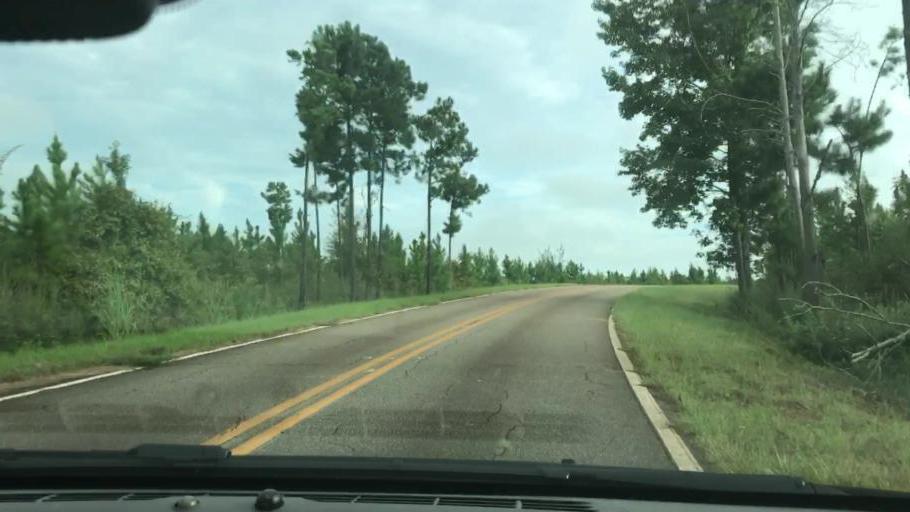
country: US
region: Georgia
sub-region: Stewart County
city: Lumpkin
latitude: 32.0596
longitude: -84.9038
